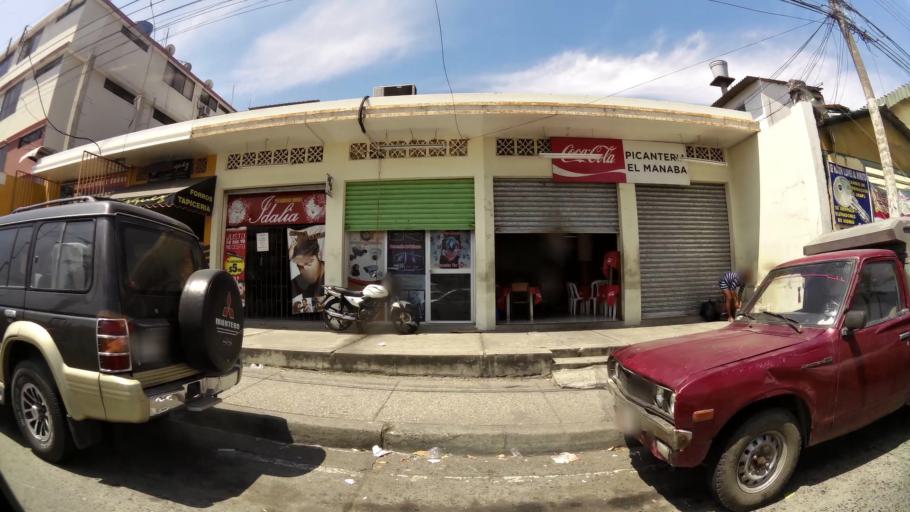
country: EC
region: Guayas
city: Eloy Alfaro
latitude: -2.1331
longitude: -79.9073
